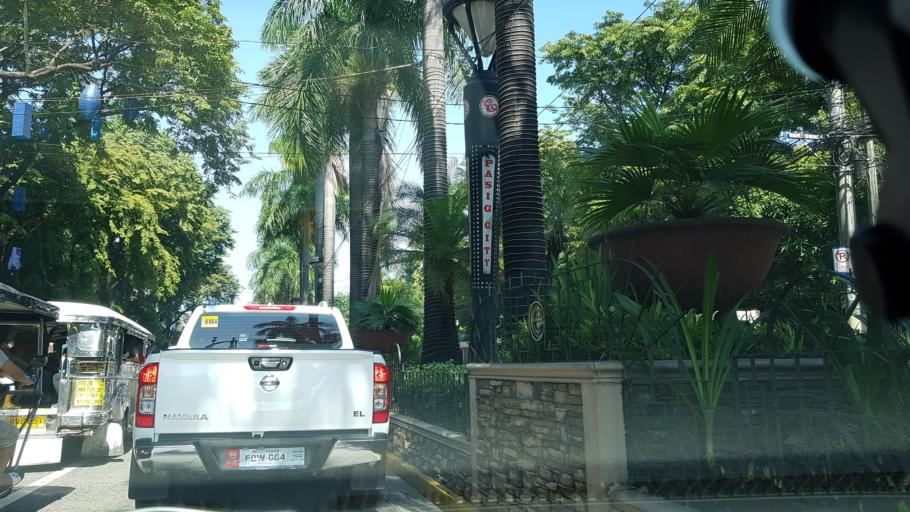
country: PH
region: Calabarzon
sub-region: Province of Rizal
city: Pateros
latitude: 14.5603
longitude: 121.0791
